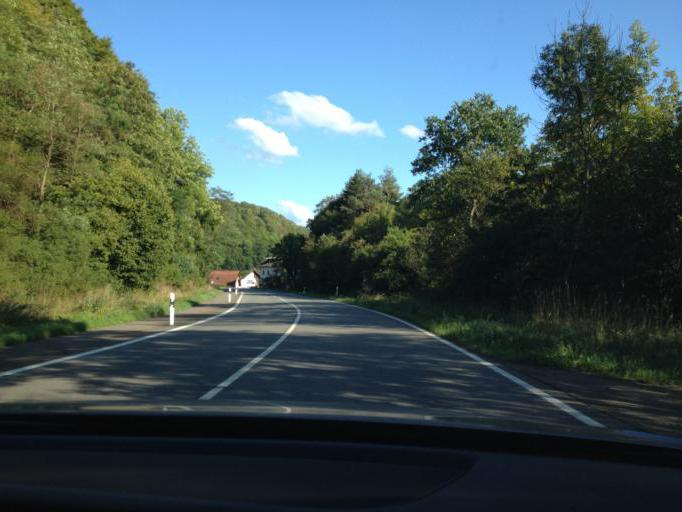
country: DE
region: Saarland
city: Schmelz
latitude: 49.4893
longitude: 6.8567
